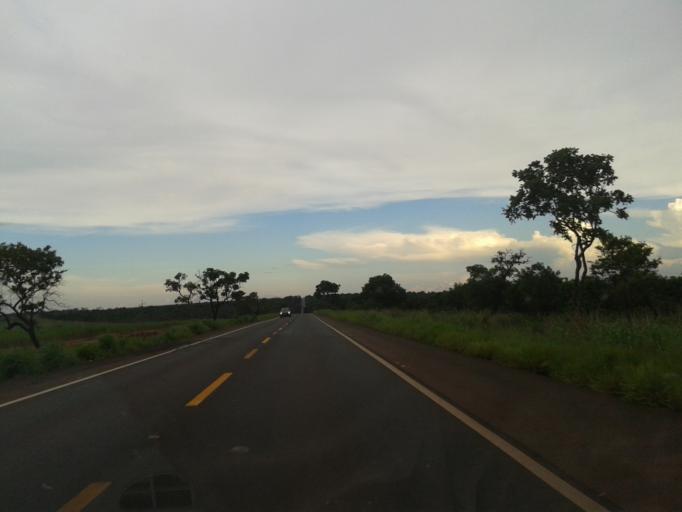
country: BR
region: Minas Gerais
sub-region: Santa Vitoria
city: Santa Vitoria
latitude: -18.8933
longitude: -50.1704
